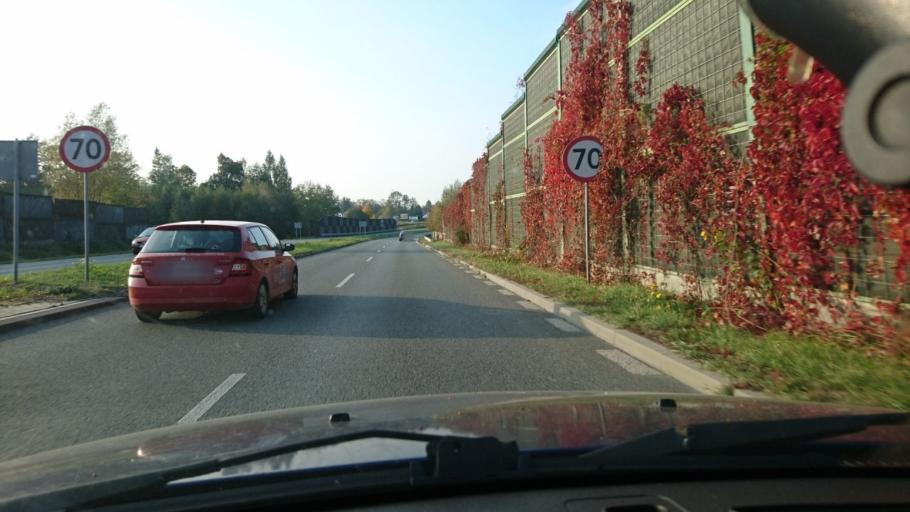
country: PL
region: Silesian Voivodeship
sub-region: Powiat cieszynski
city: Ustron
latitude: 49.7177
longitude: 18.8001
